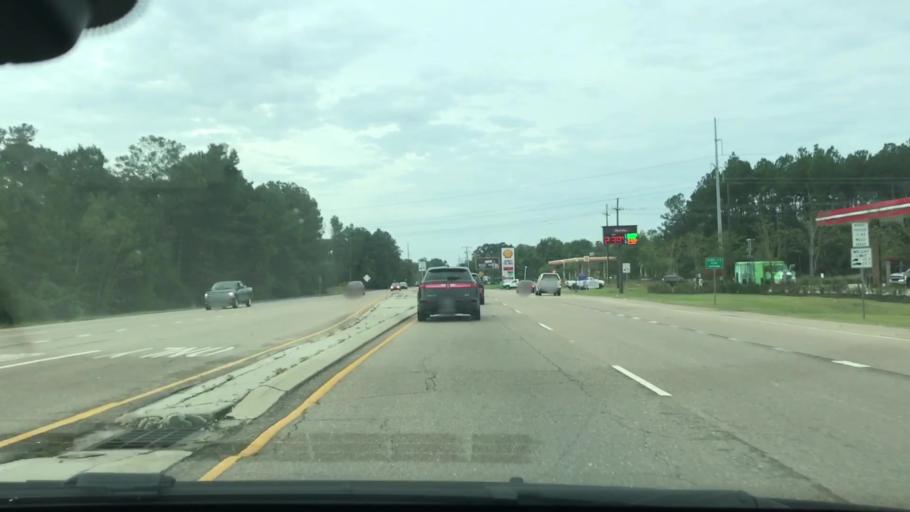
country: US
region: Louisiana
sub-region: Saint Tammany Parish
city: Slidell
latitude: 30.3075
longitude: -89.7719
